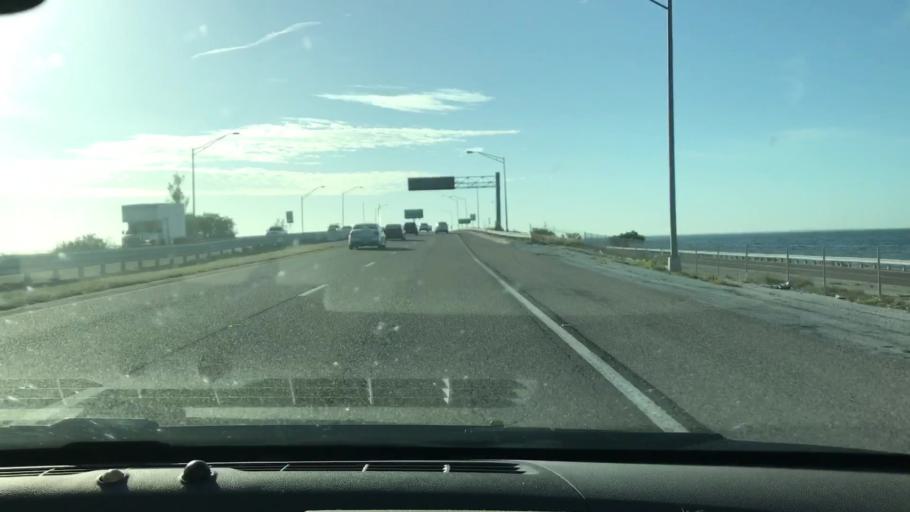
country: US
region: Florida
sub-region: Pinellas County
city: Tierra Verde
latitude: 27.6435
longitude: -82.6720
